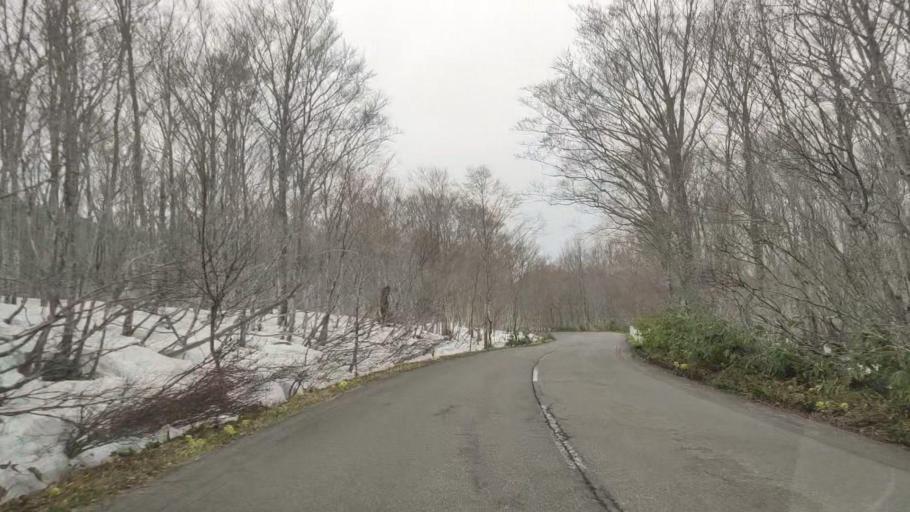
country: JP
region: Aomori
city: Aomori Shi
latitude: 40.6507
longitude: 140.9464
